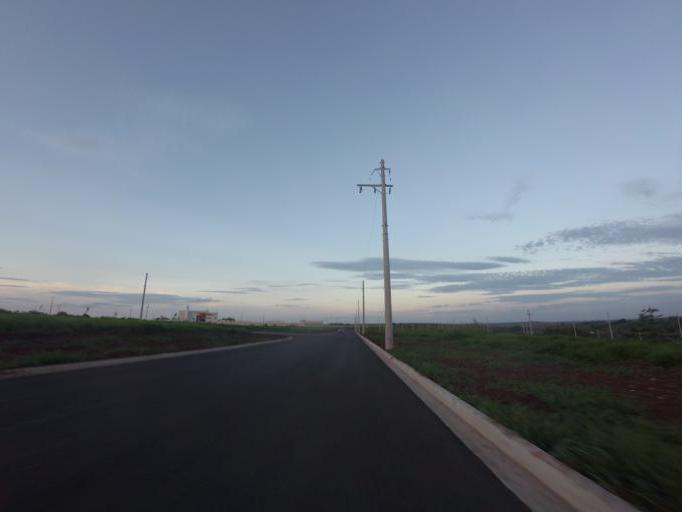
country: BR
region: Sao Paulo
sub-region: Piracicaba
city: Piracicaba
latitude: -22.7656
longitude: -47.5850
